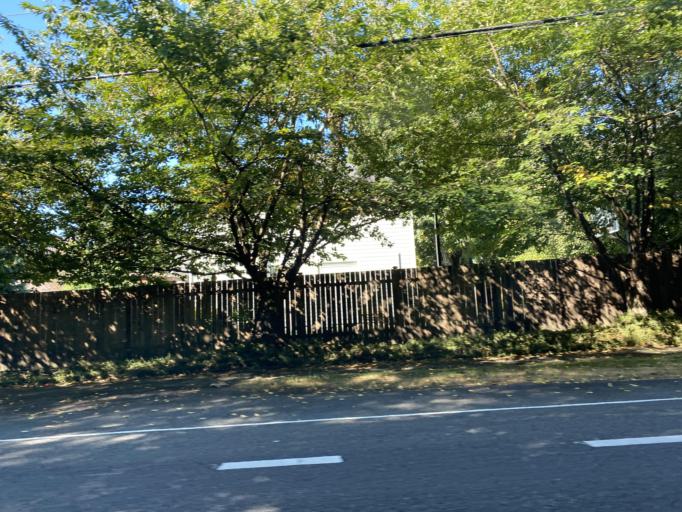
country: US
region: Washington
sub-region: Thurston County
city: Olympia
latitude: 47.0120
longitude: -122.8652
